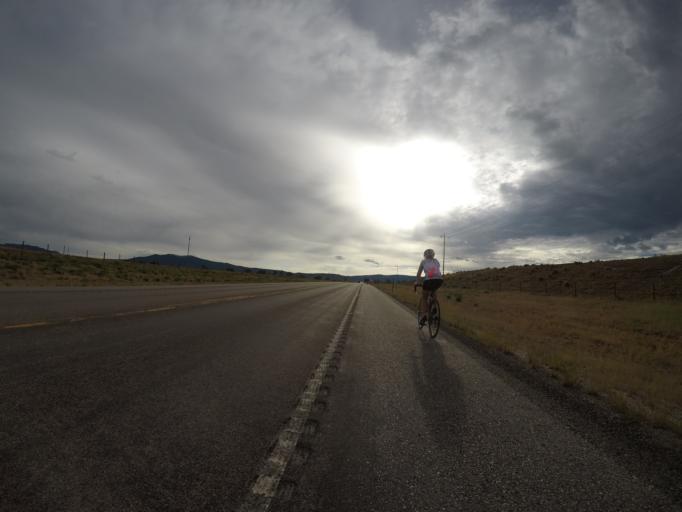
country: US
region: Wyoming
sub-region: Carbon County
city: Saratoga
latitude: 41.3495
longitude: -106.6285
